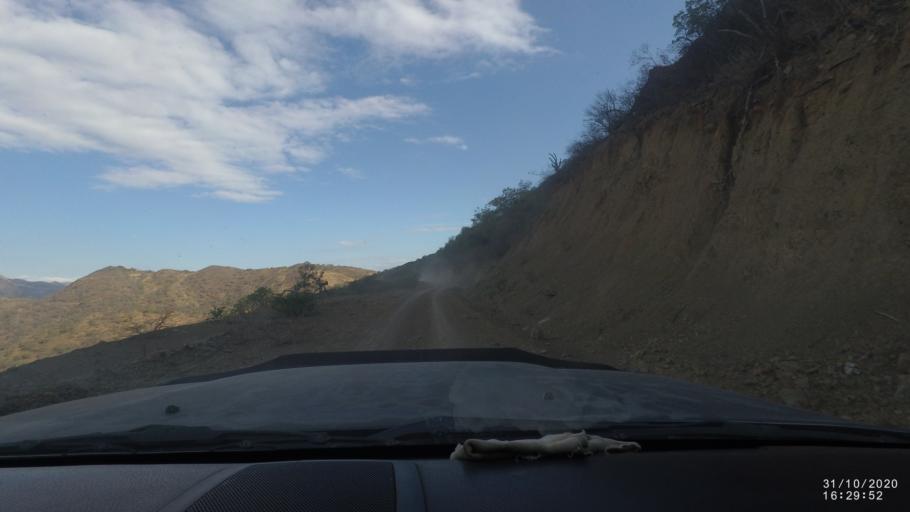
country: BO
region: Chuquisaca
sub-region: Provincia Zudanez
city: Mojocoya
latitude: -18.4229
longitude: -64.5846
